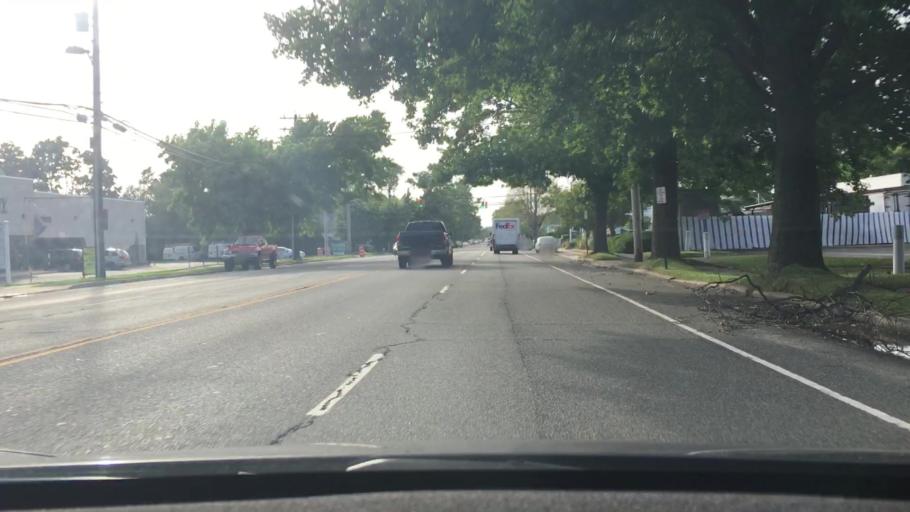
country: US
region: New York
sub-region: Nassau County
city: Hicksville
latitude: 40.7744
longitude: -73.5204
